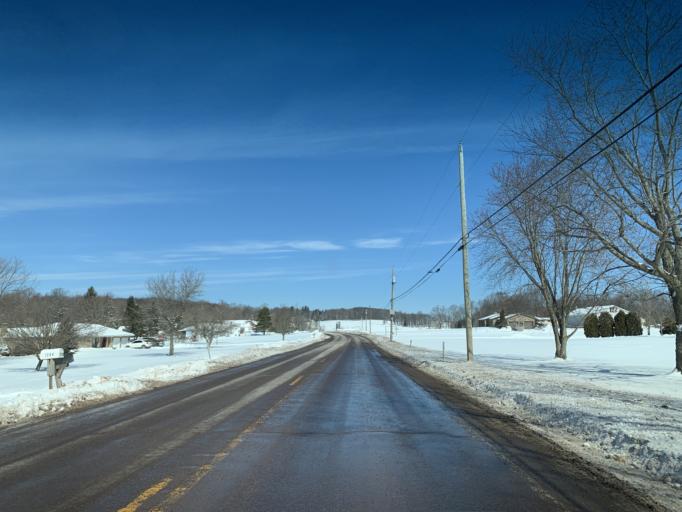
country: US
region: Pennsylvania
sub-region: Somerset County
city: Meyersdale
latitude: 39.7155
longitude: -79.1599
